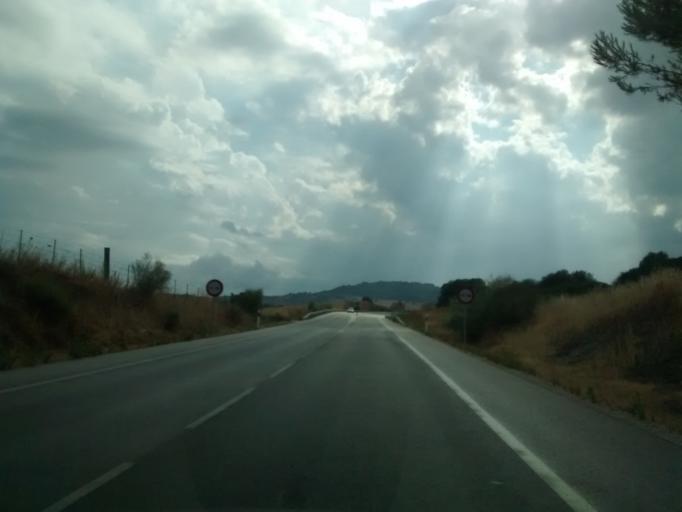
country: ES
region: Andalusia
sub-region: Provincia de Cadiz
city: El Bosque
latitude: 36.7534
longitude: -5.5230
